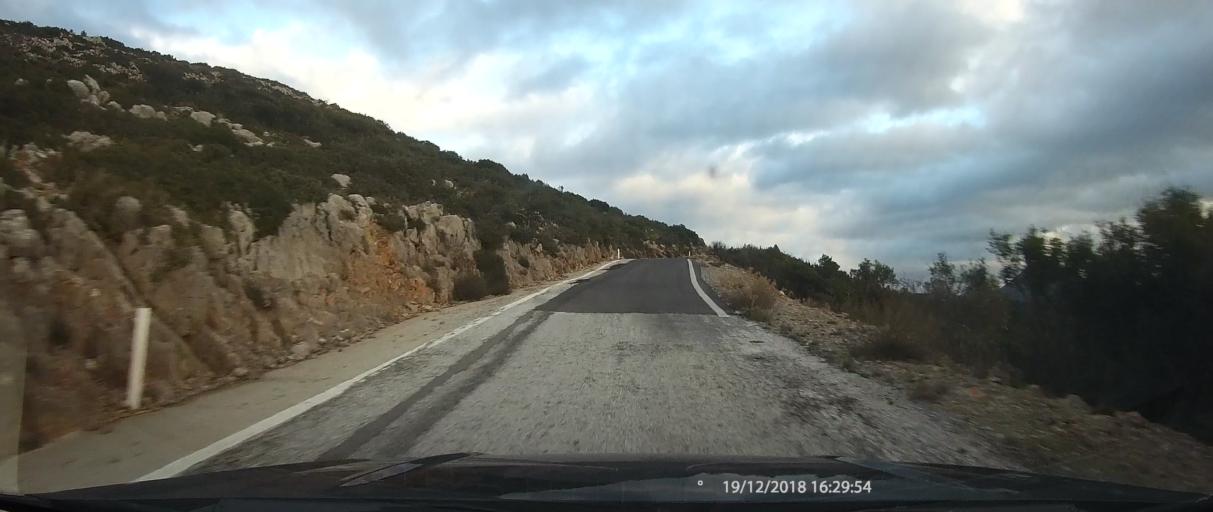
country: GR
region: Peloponnese
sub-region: Nomos Lakonias
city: Molaoi
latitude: 36.9626
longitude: 22.8779
